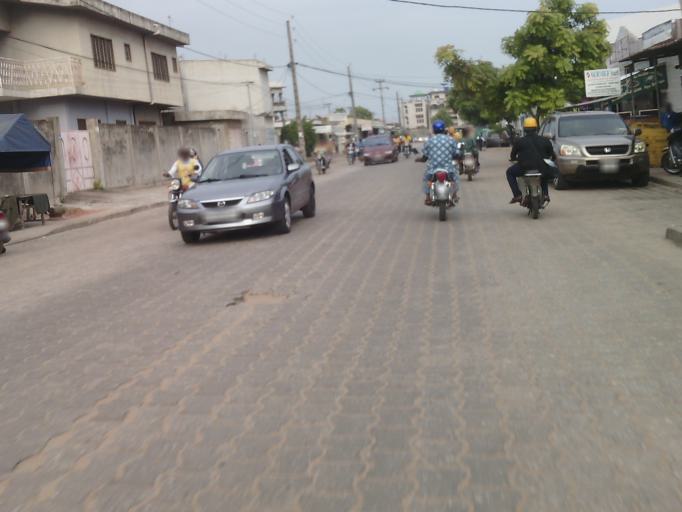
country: BJ
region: Littoral
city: Cotonou
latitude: 6.3866
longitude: 2.3821
